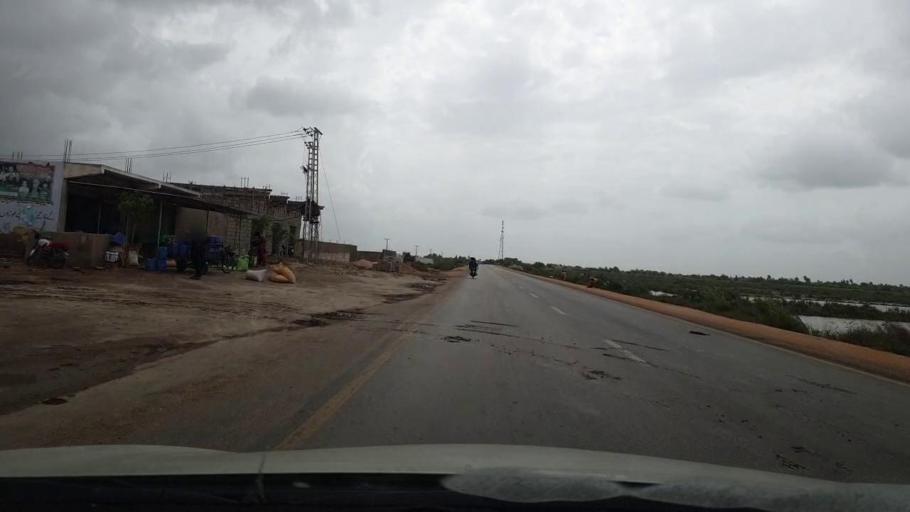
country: PK
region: Sindh
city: Mirpur Batoro
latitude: 24.6195
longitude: 68.3023
